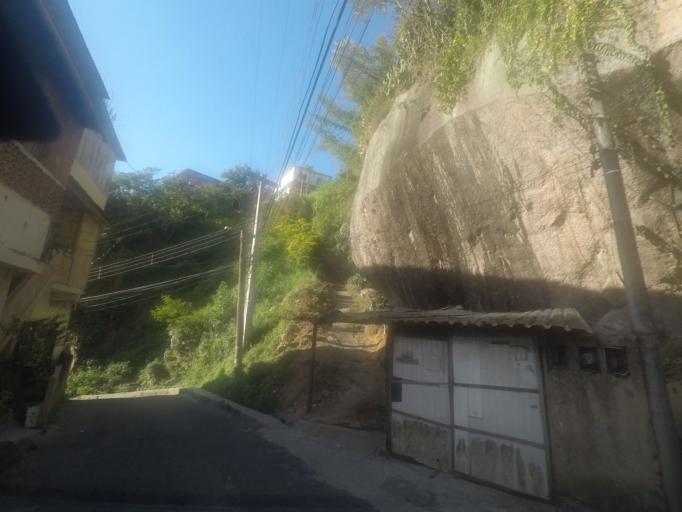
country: BR
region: Rio de Janeiro
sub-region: Petropolis
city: Petropolis
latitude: -22.4987
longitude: -43.1463
